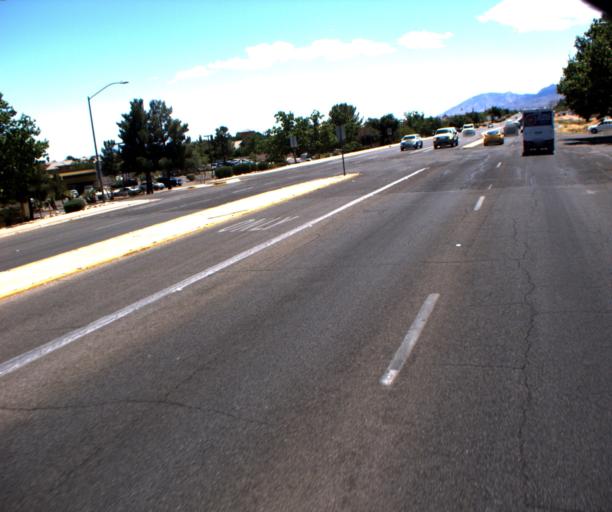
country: US
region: Arizona
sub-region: Cochise County
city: Sierra Vista
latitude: 31.5532
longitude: -110.2574
